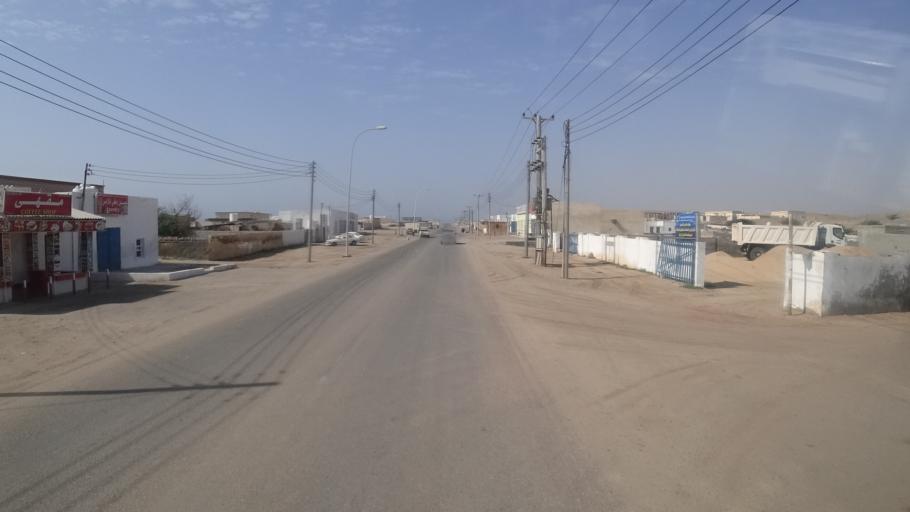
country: OM
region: Ash Sharqiyah
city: Sur
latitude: 22.1779
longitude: 59.7616
